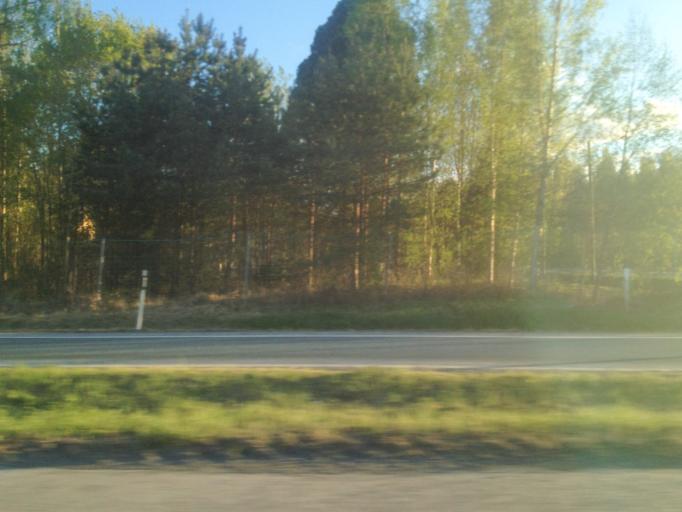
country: FI
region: Haeme
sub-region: Haemeenlinna
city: Parola
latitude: 61.0488
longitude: 24.3578
